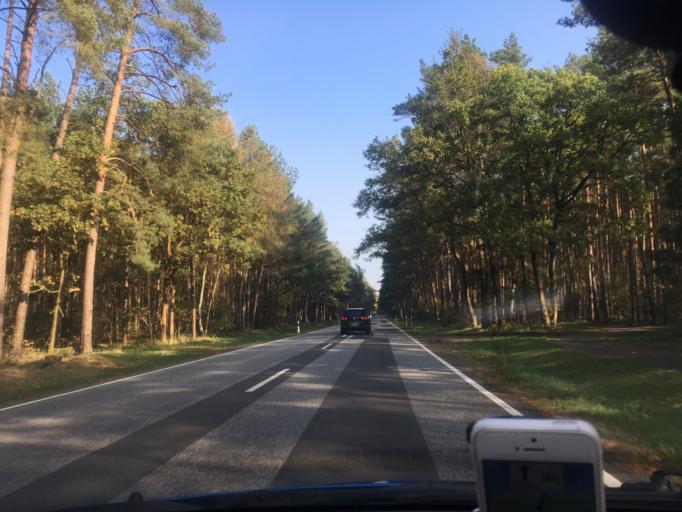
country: DE
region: Mecklenburg-Vorpommern
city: Hagenow
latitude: 53.4748
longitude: 11.2498
